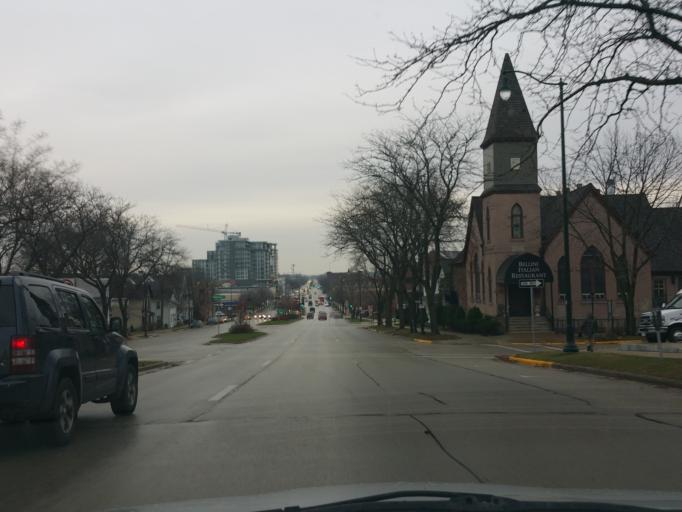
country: US
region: Wisconsin
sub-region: Dane County
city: Madison
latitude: 43.0770
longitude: -89.3806
